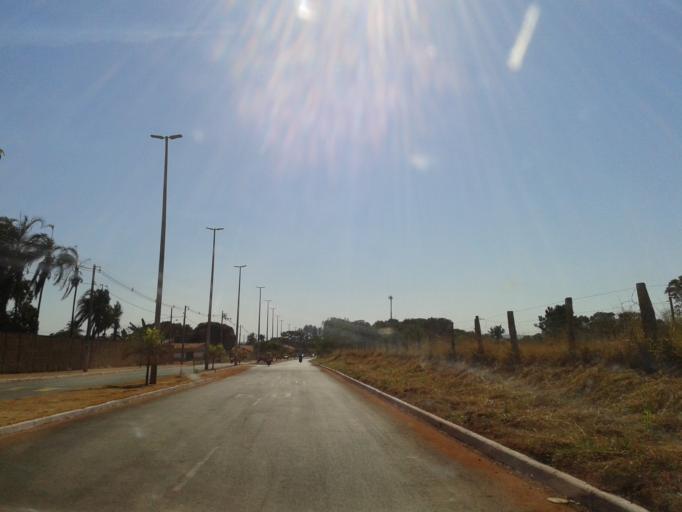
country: BR
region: Minas Gerais
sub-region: Ituiutaba
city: Ituiutaba
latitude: -18.9754
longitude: -49.4408
